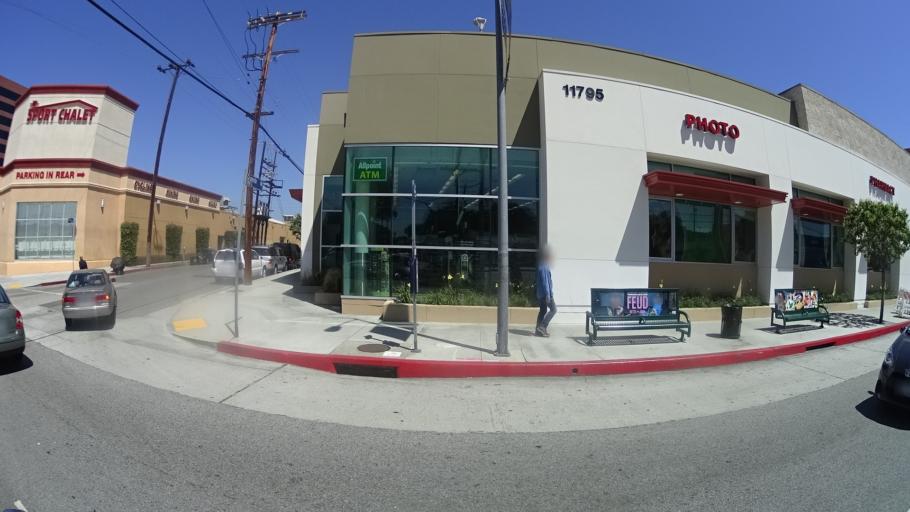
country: US
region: California
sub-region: Los Angeles County
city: Westwood, Los Angeles
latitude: 34.0333
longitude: -118.4497
